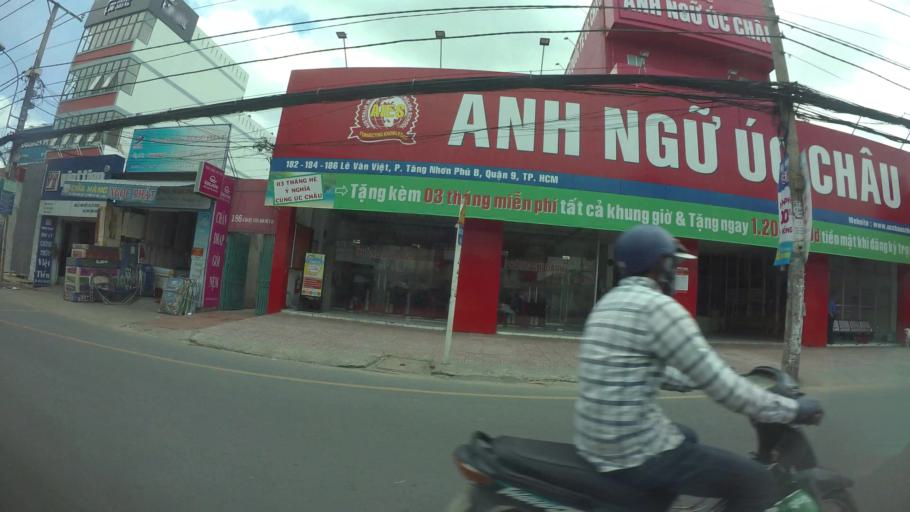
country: VN
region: Ho Chi Minh City
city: Thu Duc
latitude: 10.8444
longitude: 106.7815
